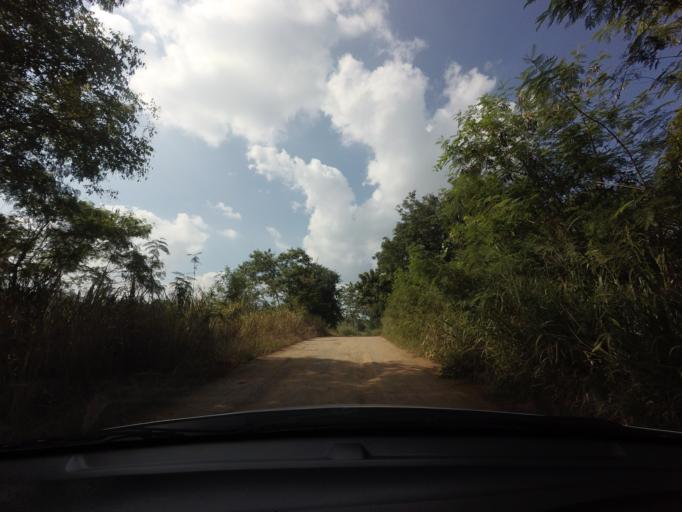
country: TH
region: Nakhon Ratchasima
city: Wang Nam Khiao
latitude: 14.4996
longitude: 101.6305
